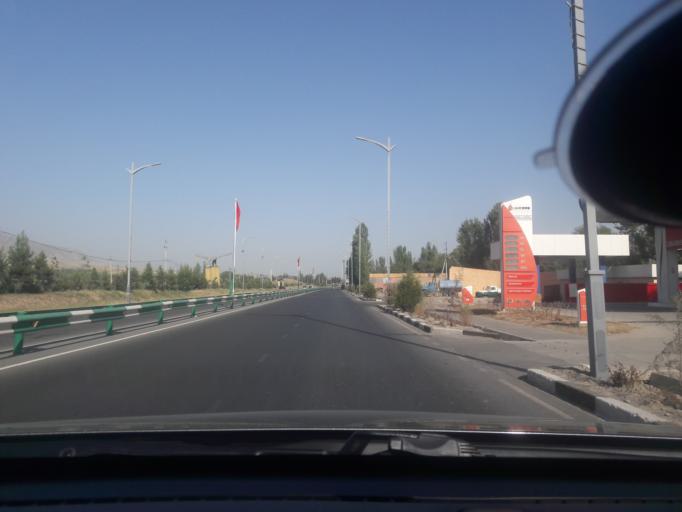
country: TJ
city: Shahrinav
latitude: 38.5764
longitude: 68.3374
